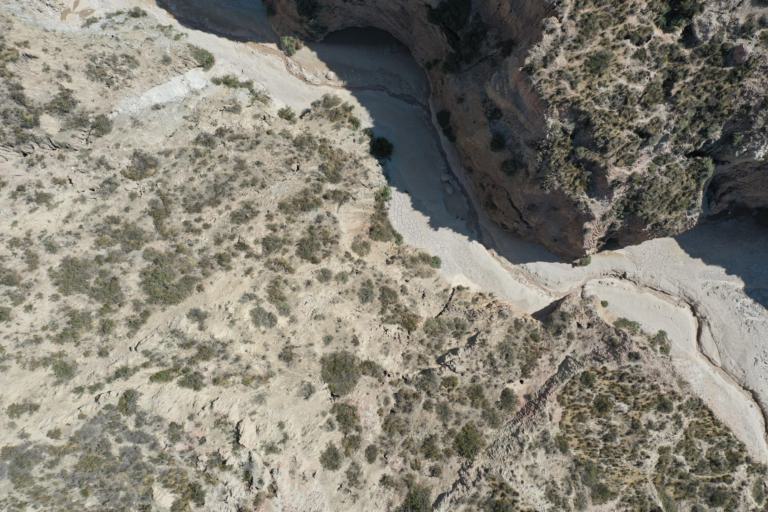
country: BO
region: La Paz
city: La Paz
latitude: -16.5601
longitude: -68.1294
